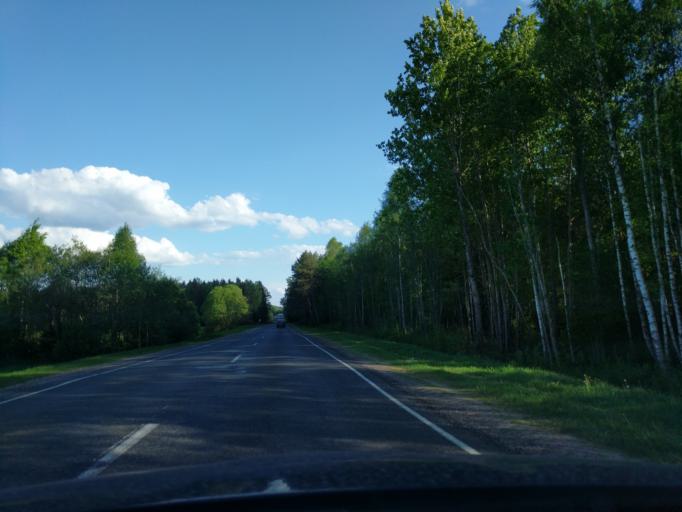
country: BY
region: Minsk
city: Kryvichy
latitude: 54.6132
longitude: 27.1767
